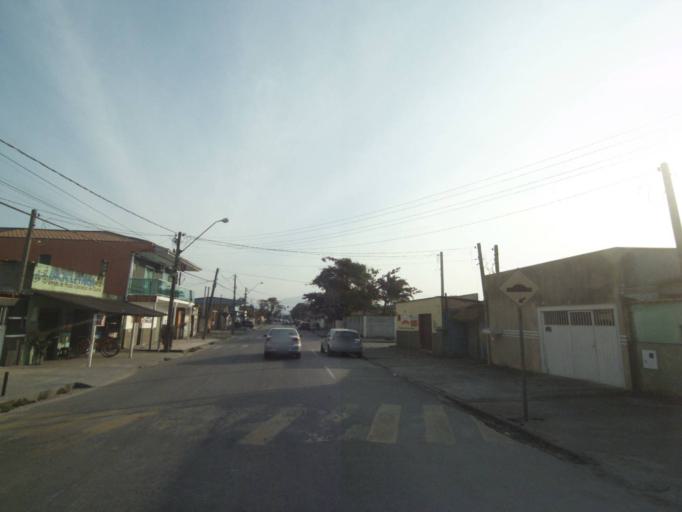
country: BR
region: Parana
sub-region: Paranagua
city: Paranagua
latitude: -25.5194
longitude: -48.5338
